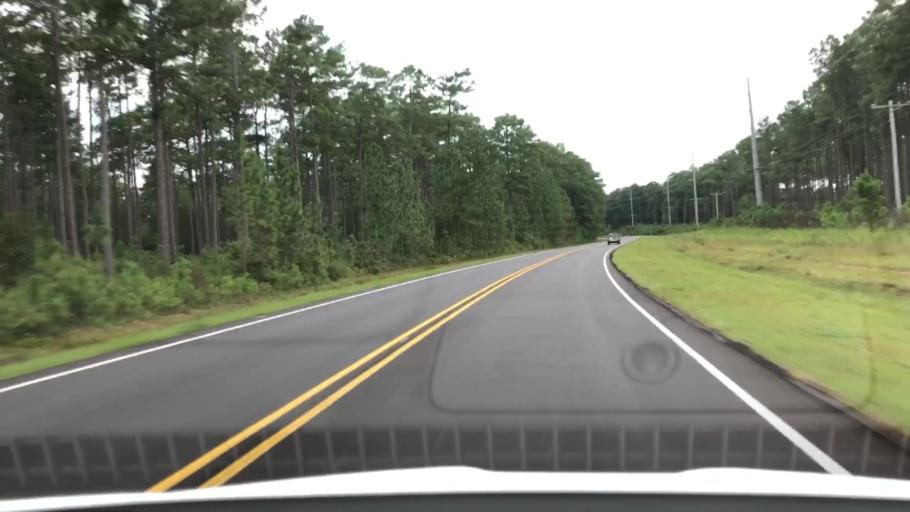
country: US
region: North Carolina
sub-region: Jones County
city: Maysville
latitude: 34.8184
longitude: -77.1466
